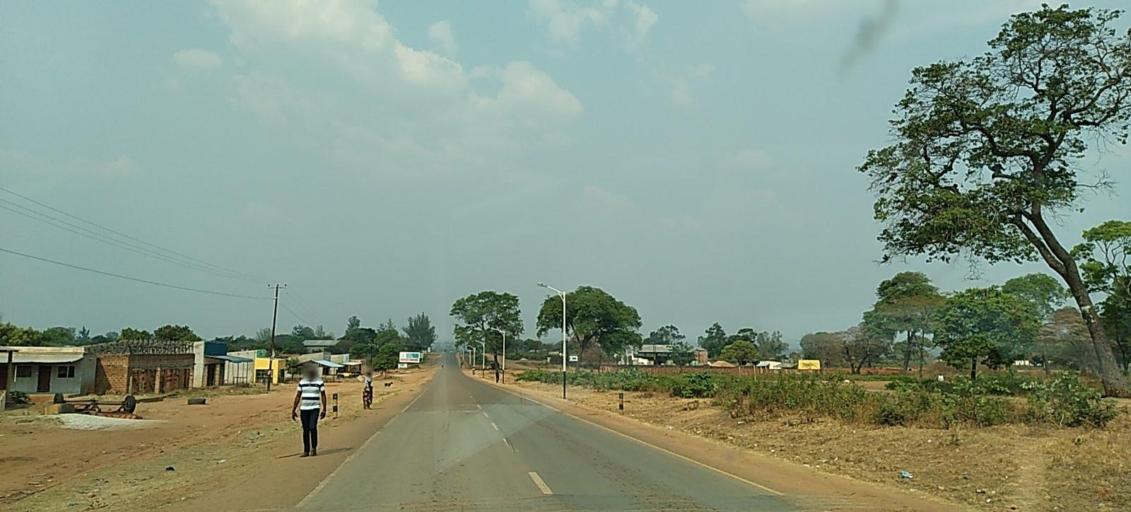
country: ZM
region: North-Western
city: Kabompo
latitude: -13.5933
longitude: 24.2031
